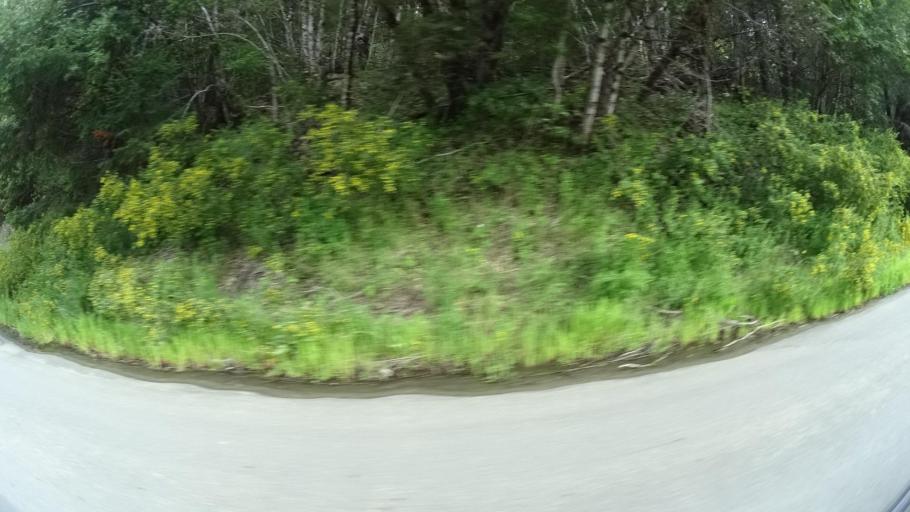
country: US
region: California
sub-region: Humboldt County
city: Redway
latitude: 40.2957
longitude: -123.8314
